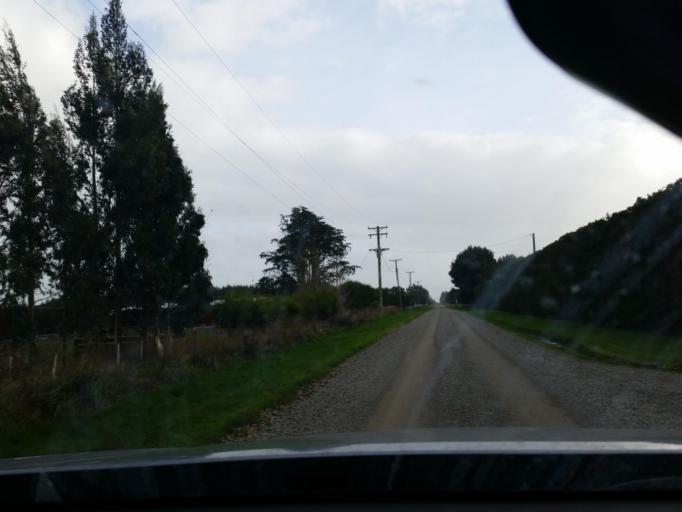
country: NZ
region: Southland
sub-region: Invercargill City
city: Invercargill
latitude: -46.3222
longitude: 168.3716
